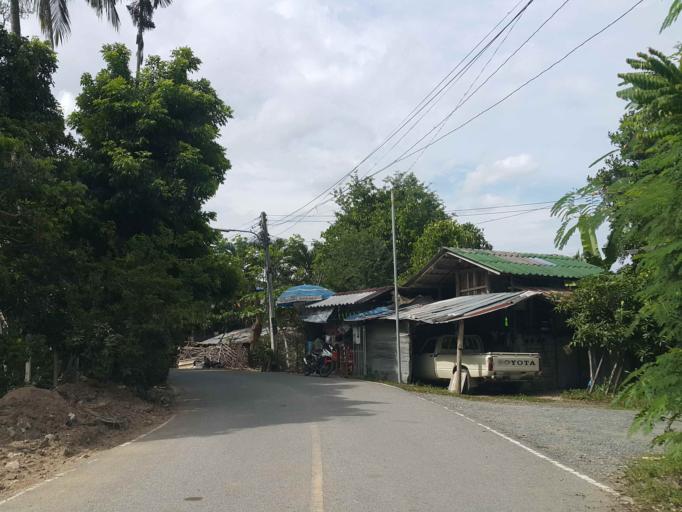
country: TH
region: Chiang Mai
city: Saraphi
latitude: 18.7371
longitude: 99.0570
